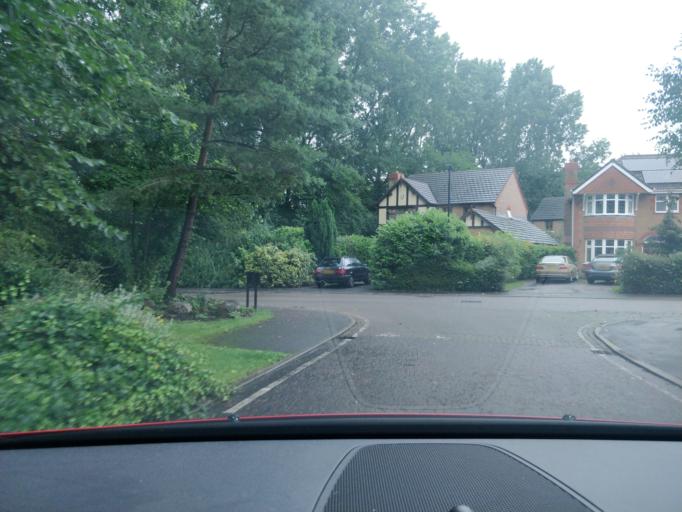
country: GB
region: England
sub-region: Lancashire
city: Banks
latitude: 53.6770
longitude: -2.9216
